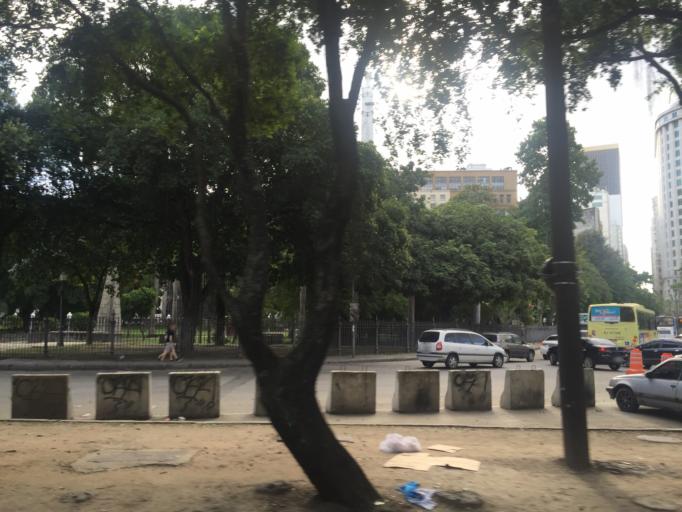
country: BR
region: Rio de Janeiro
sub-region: Rio De Janeiro
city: Rio de Janeiro
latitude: -22.9137
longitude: -43.1754
